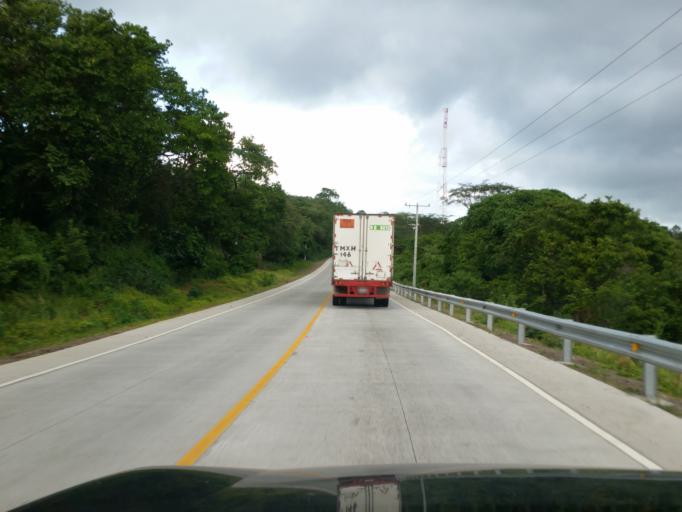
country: NI
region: Managua
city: Ciudad Sandino
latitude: 12.0831
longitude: -86.3918
